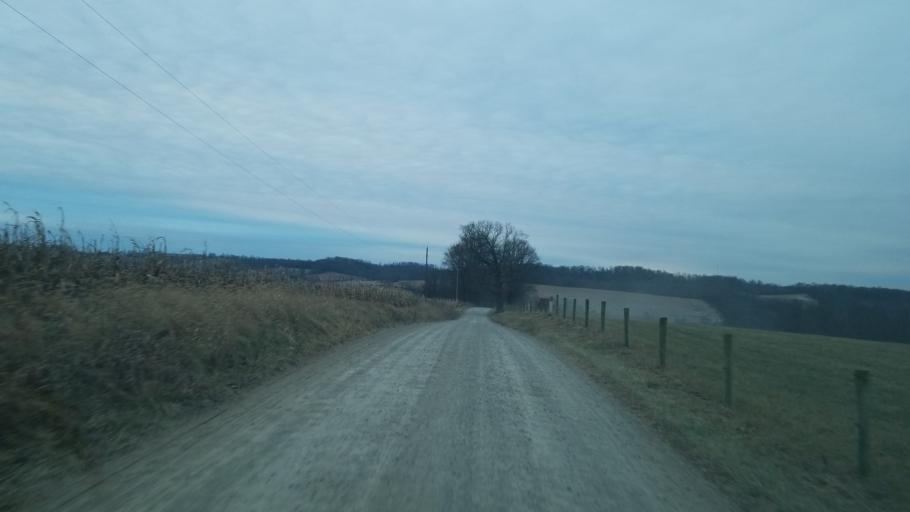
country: US
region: Ohio
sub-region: Holmes County
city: Millersburg
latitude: 40.4606
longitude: -81.8488
